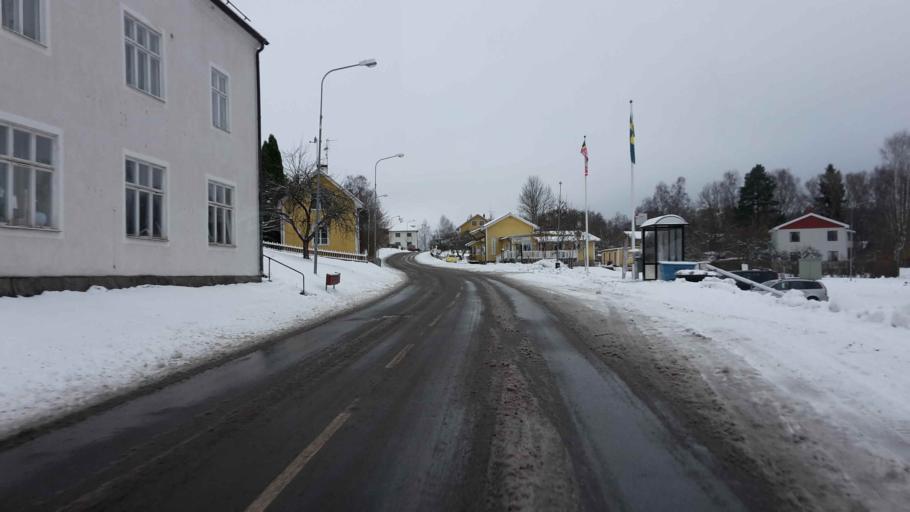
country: SE
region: Kalmar
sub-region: Vasterviks Kommun
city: Overum
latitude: 58.1435
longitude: 16.2052
